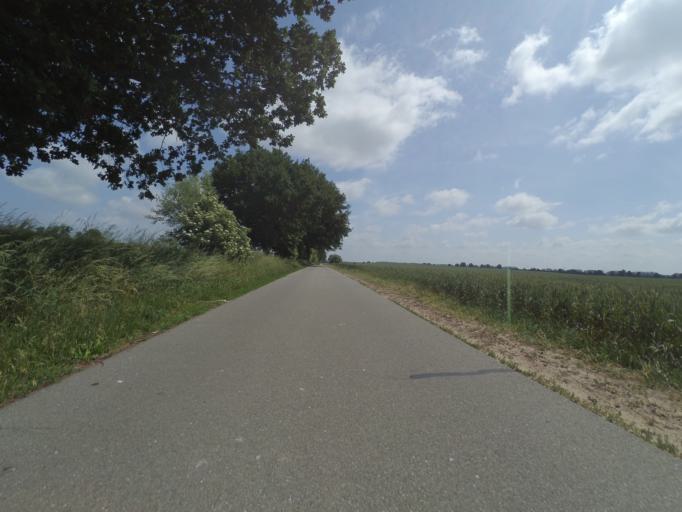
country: DE
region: Mecklenburg-Vorpommern
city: Siggelkow
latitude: 53.4085
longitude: 11.9942
